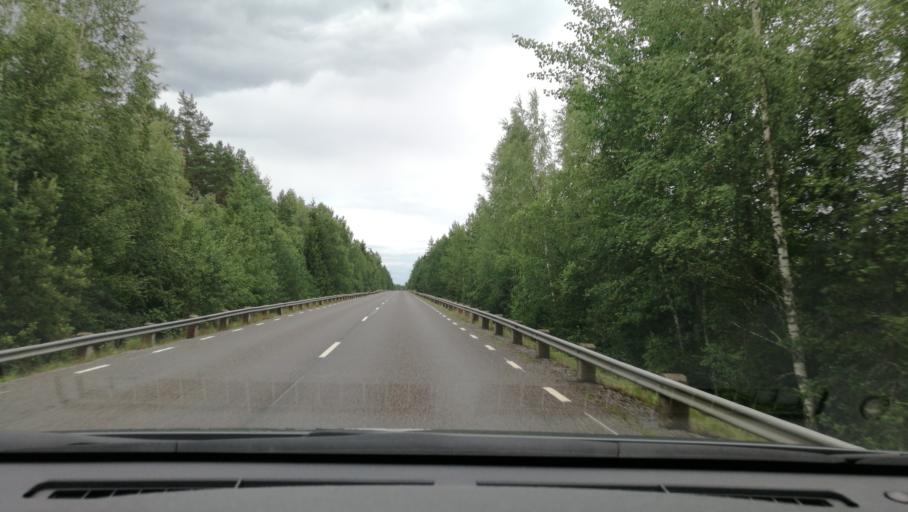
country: SE
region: OEstergoetland
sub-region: Norrkopings Kommun
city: Svartinge
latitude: 58.7992
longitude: 15.9474
